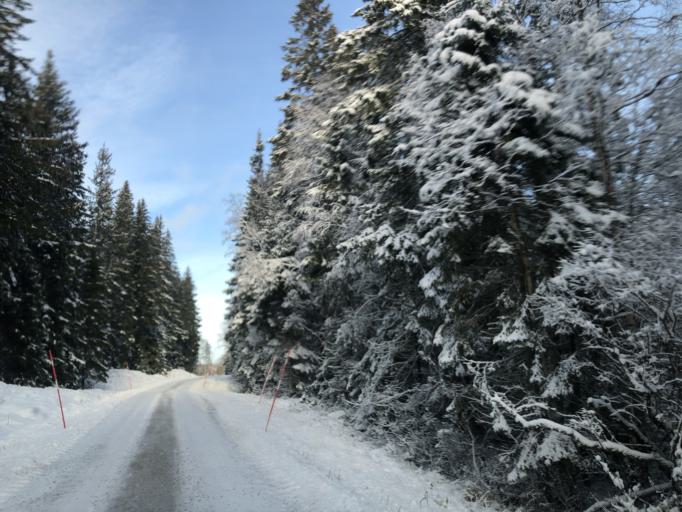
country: SE
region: Vaestra Goetaland
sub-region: Ulricehamns Kommun
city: Ulricehamn
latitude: 57.7509
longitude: 13.5095
